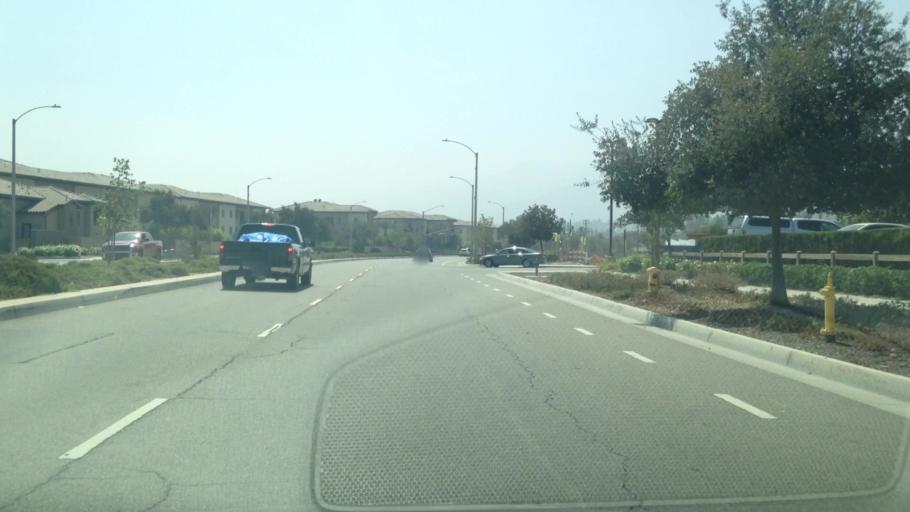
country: US
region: California
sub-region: Riverside County
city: El Cerrito
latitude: 33.8117
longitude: -117.5053
